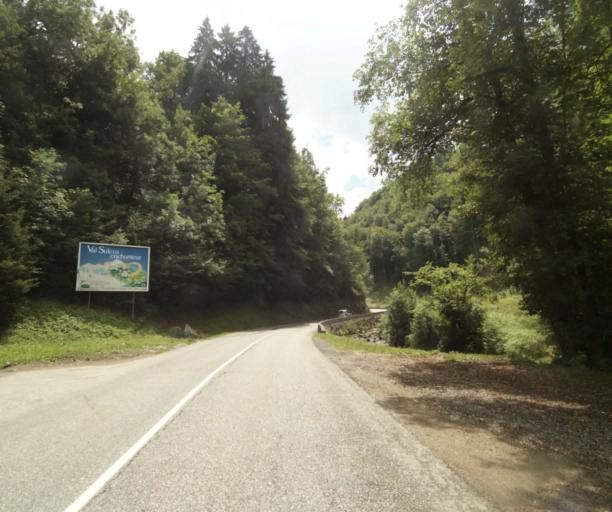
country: FR
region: Rhone-Alpes
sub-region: Departement de la Haute-Savoie
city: Thones
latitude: 45.8615
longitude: 6.3273
